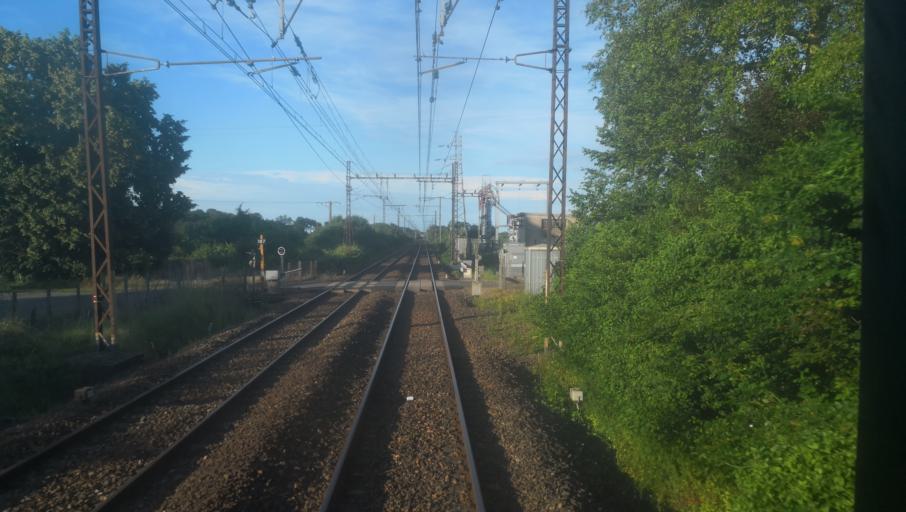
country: FR
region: Centre
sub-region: Departement de l'Indre
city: Montierchaume
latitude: 46.8608
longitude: 1.8189
